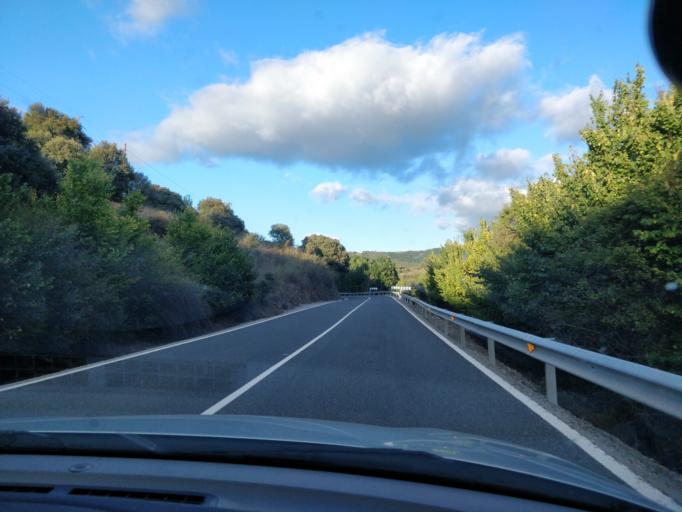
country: ES
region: Castille and Leon
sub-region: Provincia de Leon
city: Borrenes
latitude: 42.4906
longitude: -6.7438
